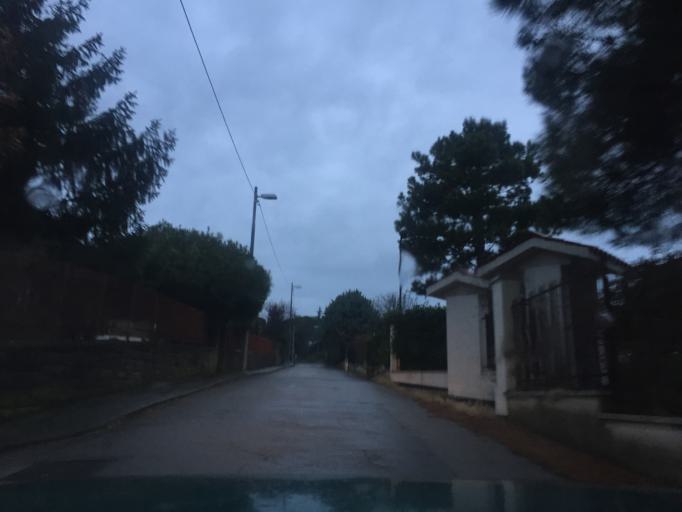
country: IT
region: Friuli Venezia Giulia
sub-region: Provincia di Trieste
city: Muggia
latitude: 45.6006
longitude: 13.7569
